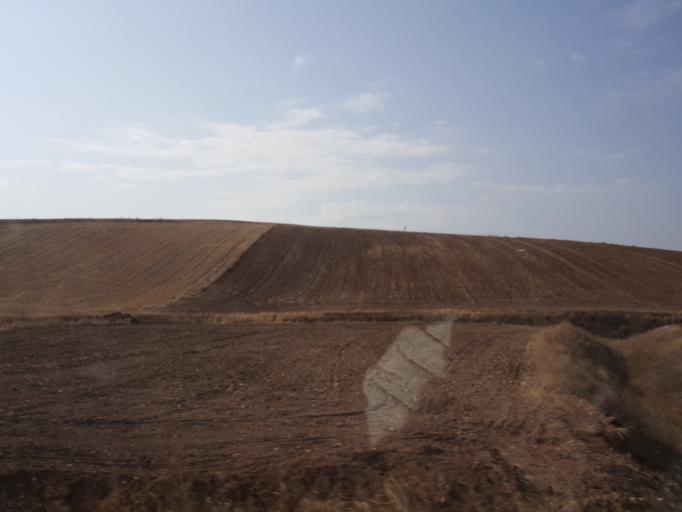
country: TR
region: Corum
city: Cemilbey
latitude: 40.1768
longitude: 35.0330
